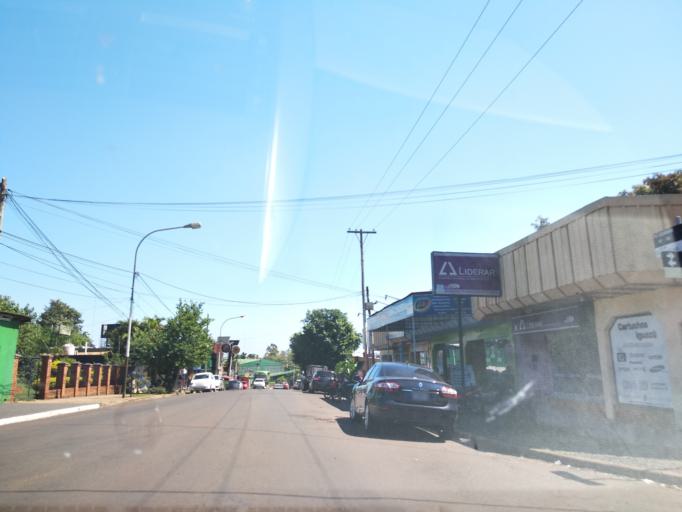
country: AR
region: Misiones
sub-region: Departamento de Iguazu
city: Puerto Iguazu
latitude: -25.5981
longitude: -54.5693
